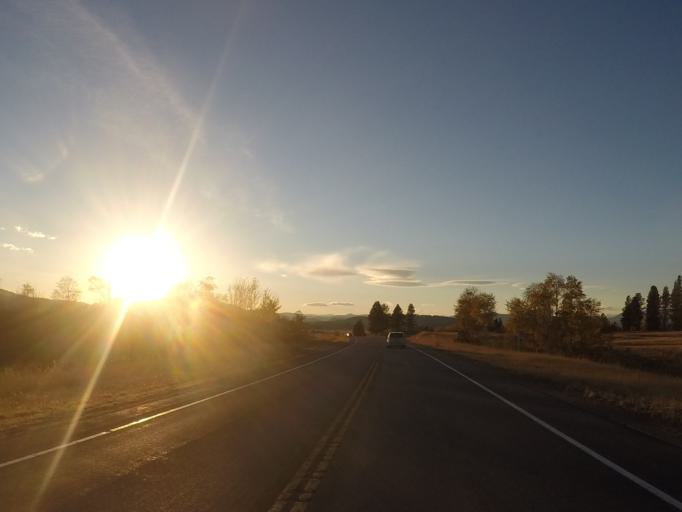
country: US
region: Montana
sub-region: Missoula County
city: Seeley Lake
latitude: 47.0199
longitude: -113.0976
